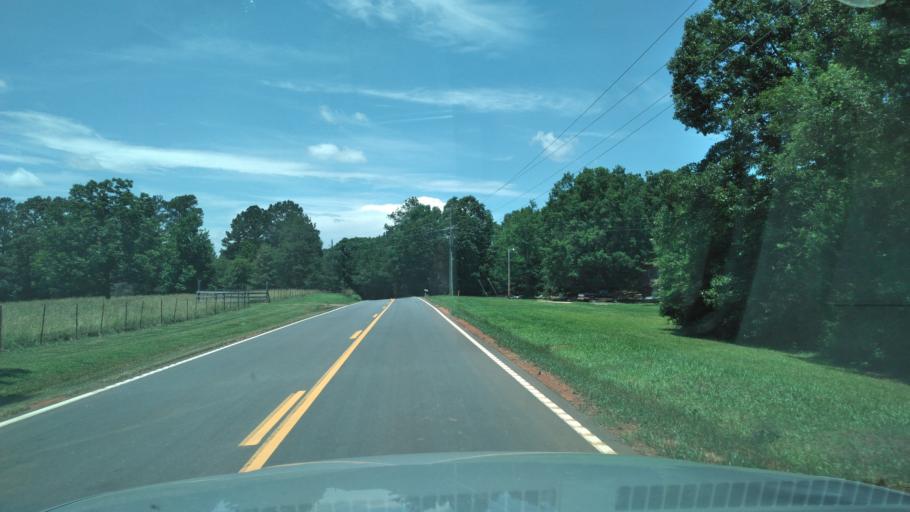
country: US
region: South Carolina
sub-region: Greenwood County
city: Ware Shoals
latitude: 34.4028
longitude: -82.1236
